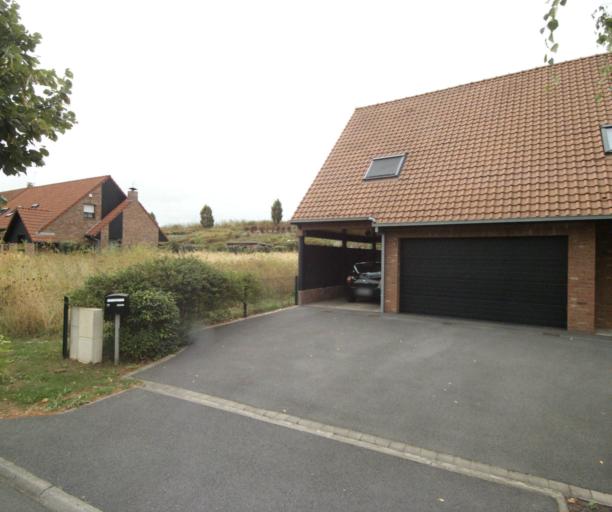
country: FR
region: Nord-Pas-de-Calais
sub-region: Departement du Nord
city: Lesquin
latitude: 50.5886
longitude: 3.1271
